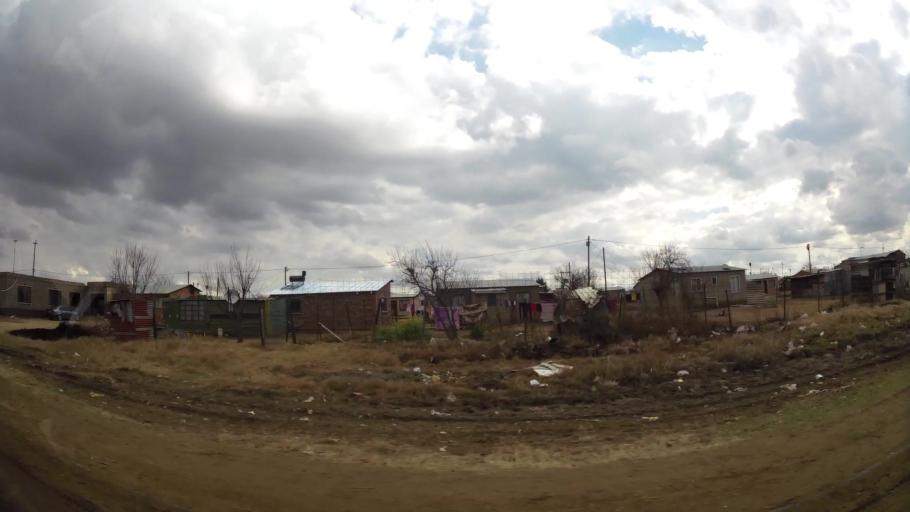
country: ZA
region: Orange Free State
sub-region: Fezile Dabi District Municipality
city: Sasolburg
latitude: -26.8763
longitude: 27.8734
